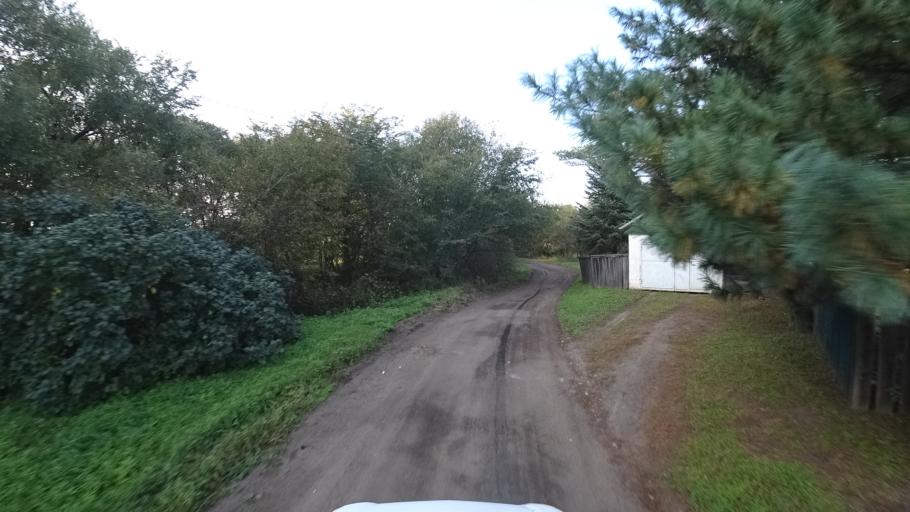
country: RU
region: Amur
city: Arkhara
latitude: 49.3630
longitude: 130.1172
